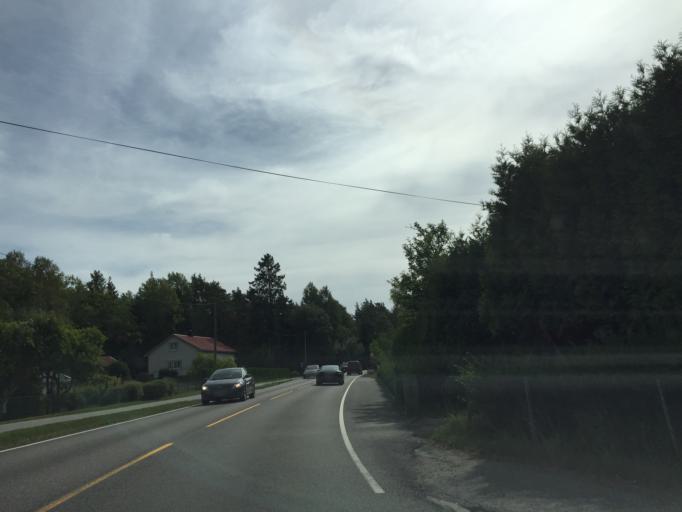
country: NO
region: Ostfold
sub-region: Fredrikstad
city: Fredrikstad
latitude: 59.1563
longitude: 10.9335
